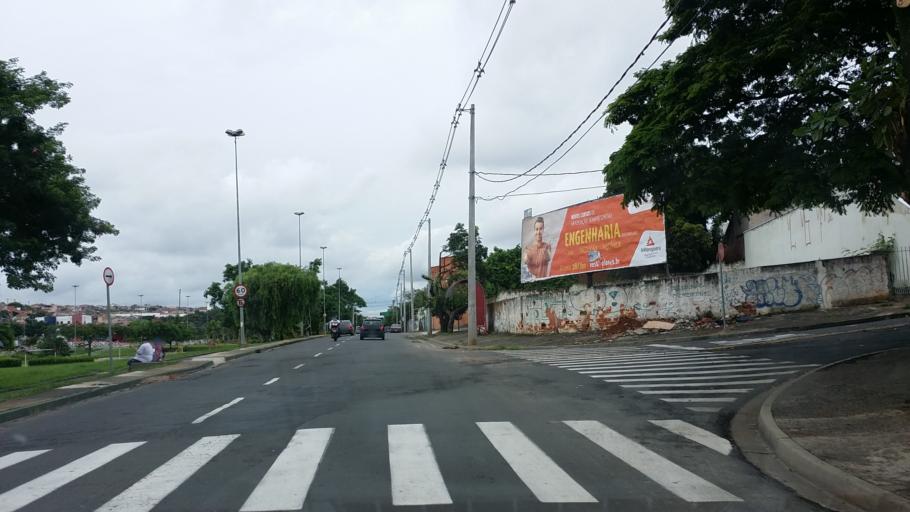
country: BR
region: Sao Paulo
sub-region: Indaiatuba
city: Indaiatuba
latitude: -23.1207
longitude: -47.2323
